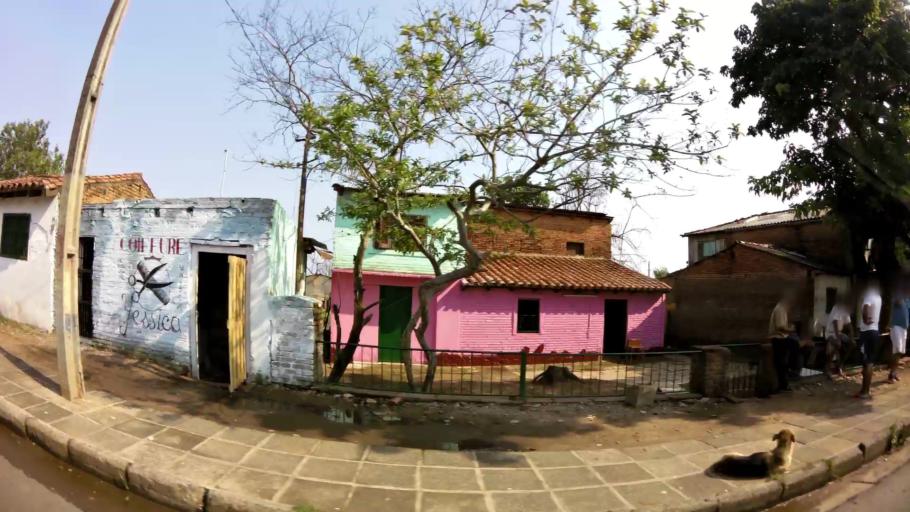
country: PY
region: Asuncion
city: Asuncion
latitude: -25.3036
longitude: -57.6670
